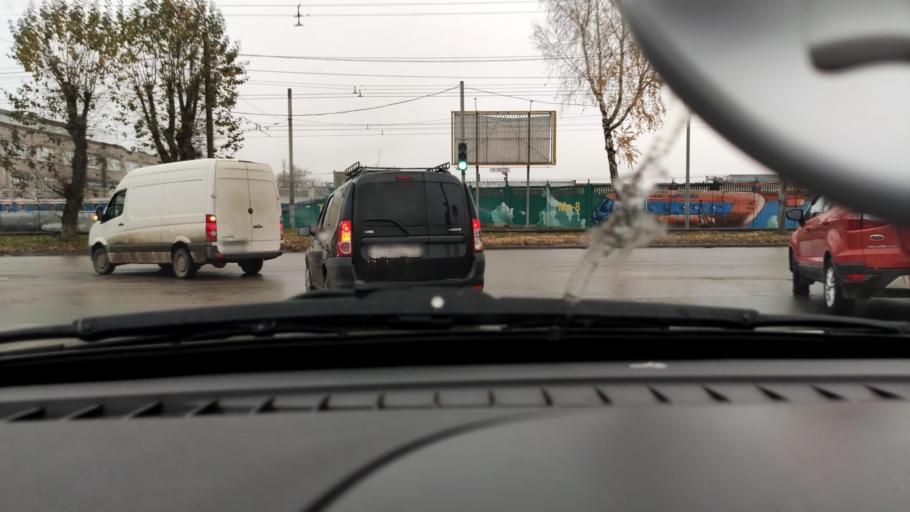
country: RU
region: Perm
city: Perm
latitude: 57.9752
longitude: 56.2460
